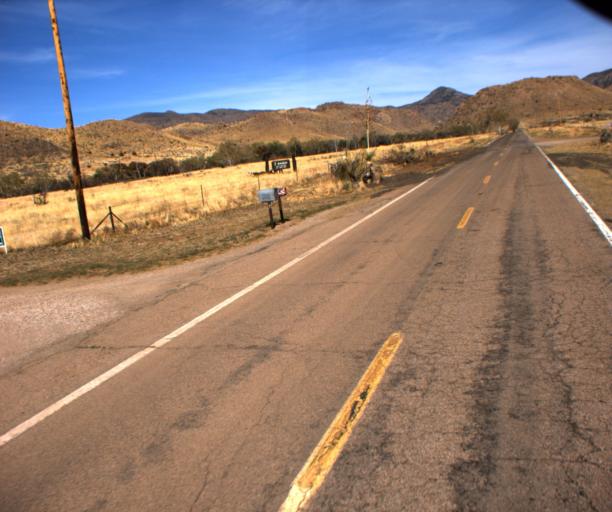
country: US
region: Arizona
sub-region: Cochise County
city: Willcox
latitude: 32.0067
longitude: -109.4062
